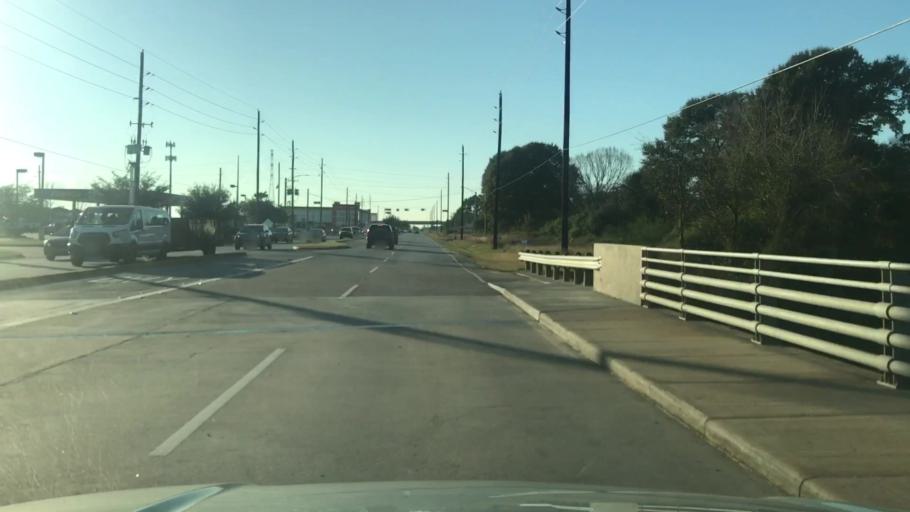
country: US
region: Texas
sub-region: Harris County
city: Katy
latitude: 29.8318
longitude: -95.7526
